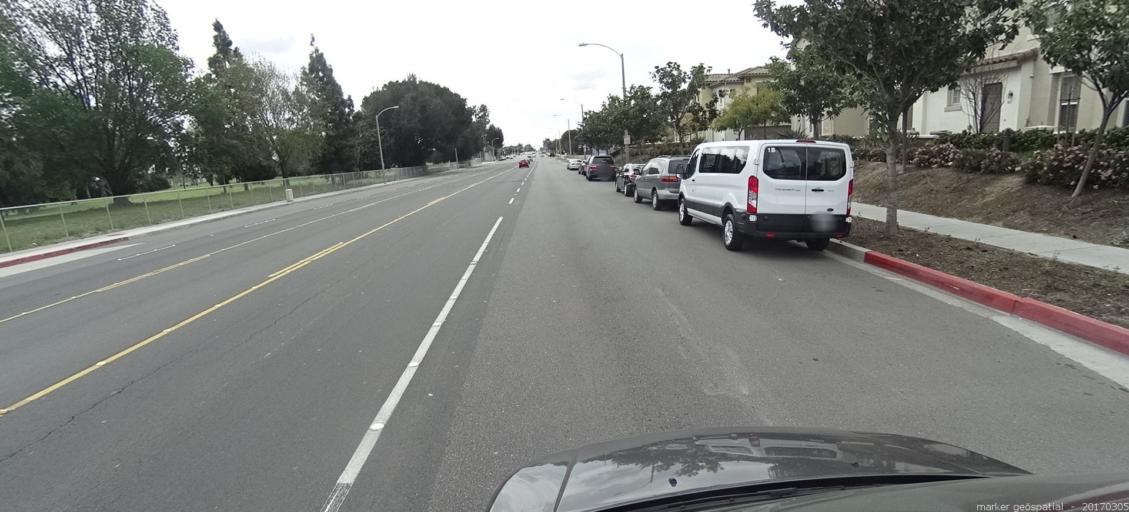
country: US
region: California
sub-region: Orange County
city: Buena Park
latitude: 33.8367
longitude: -117.9761
